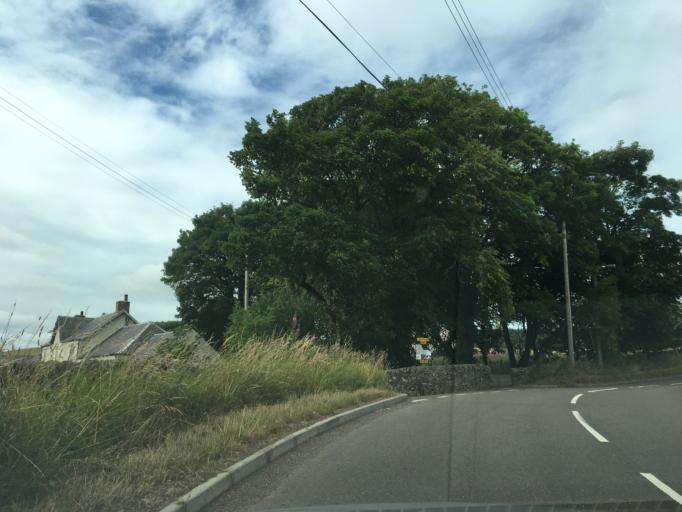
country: GB
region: Scotland
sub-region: South Lanarkshire
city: Douglas
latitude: 55.4955
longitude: -3.7755
